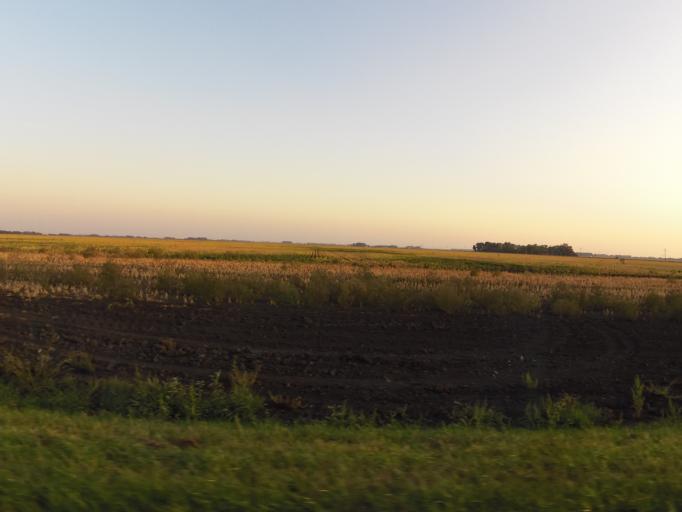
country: US
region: North Dakota
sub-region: Grand Forks County
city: Grand Forks
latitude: 47.8603
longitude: -97.0407
